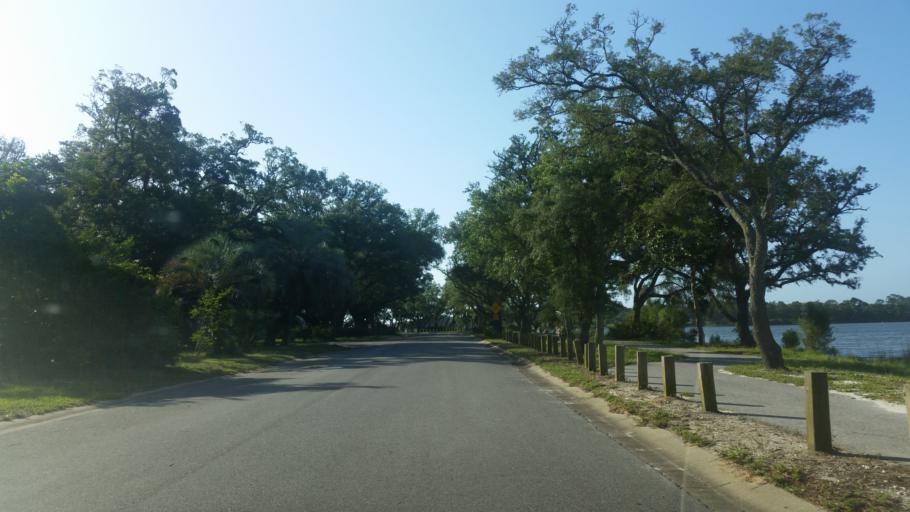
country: US
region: Florida
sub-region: Escambia County
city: Warrington
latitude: 30.3744
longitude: -87.2837
